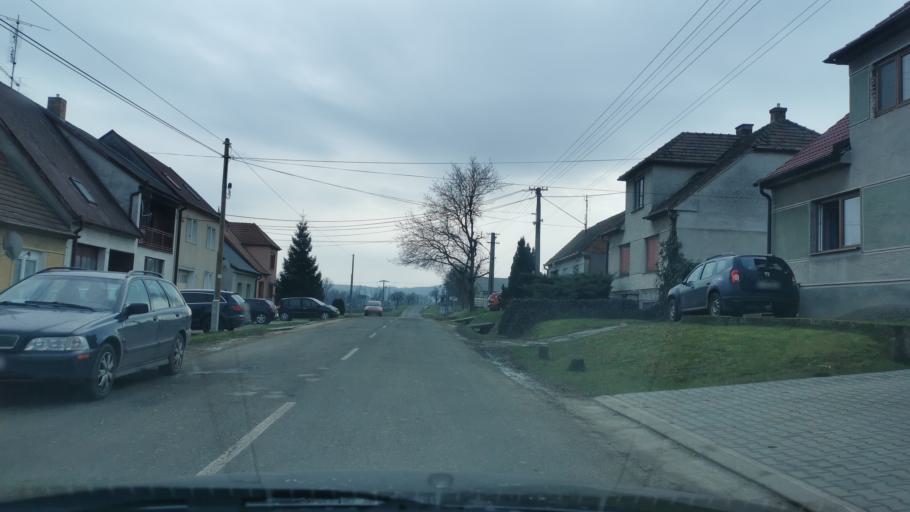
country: SK
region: Trnavsky
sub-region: Okres Skalica
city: Skalica
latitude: 48.7614
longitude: 17.2829
